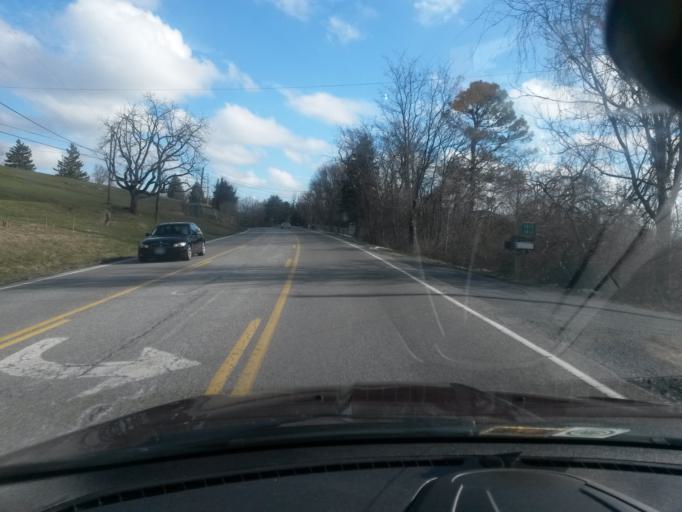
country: US
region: Virginia
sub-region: Augusta County
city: Jolivue
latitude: 38.0726
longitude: -79.1021
